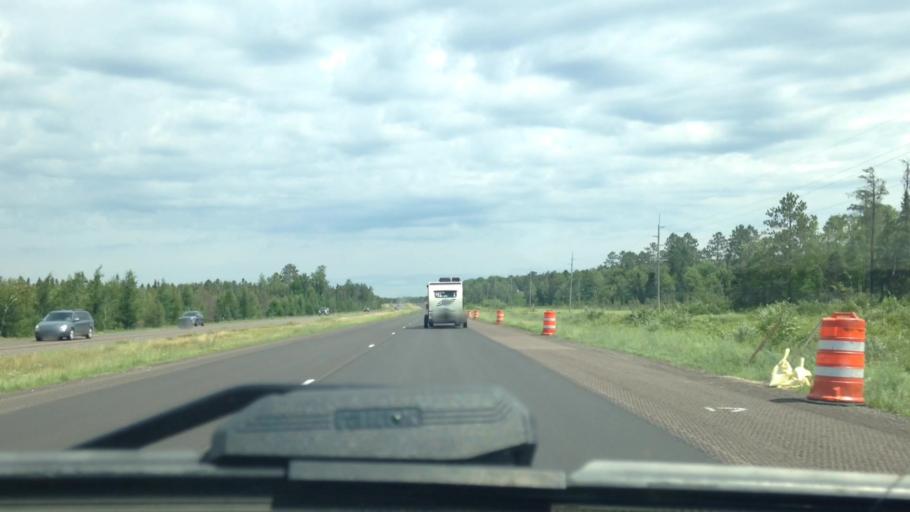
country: US
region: Wisconsin
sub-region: Washburn County
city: Spooner
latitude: 46.1648
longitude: -91.8071
